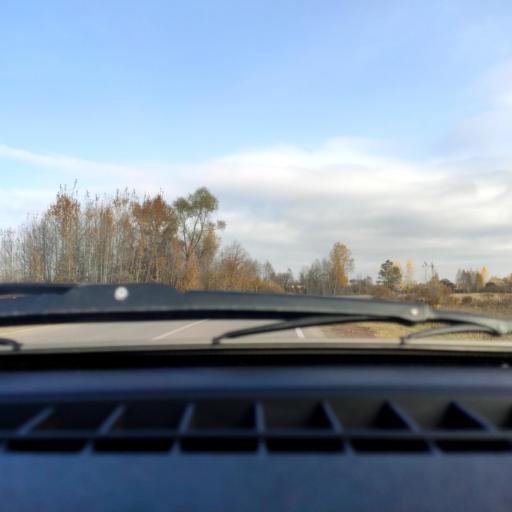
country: RU
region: Bashkortostan
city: Kabakovo
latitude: 54.7318
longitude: 56.1930
